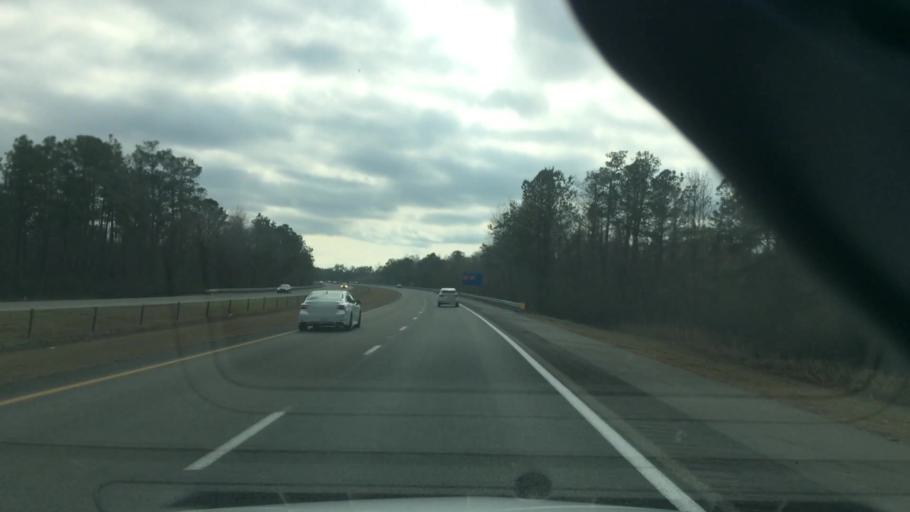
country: US
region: North Carolina
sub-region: New Hanover County
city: Castle Hayne
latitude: 34.3712
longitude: -77.8871
